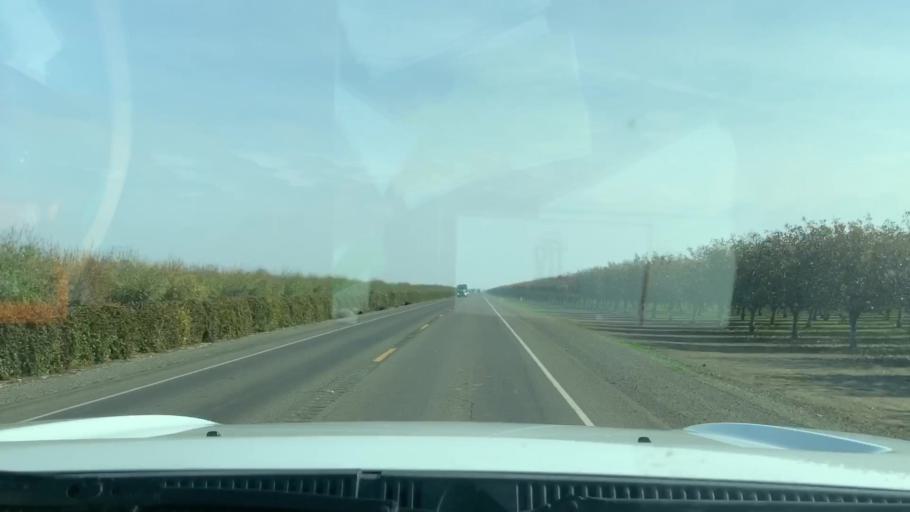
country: US
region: California
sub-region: Fresno County
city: Huron
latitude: 36.2553
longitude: -120.1172
